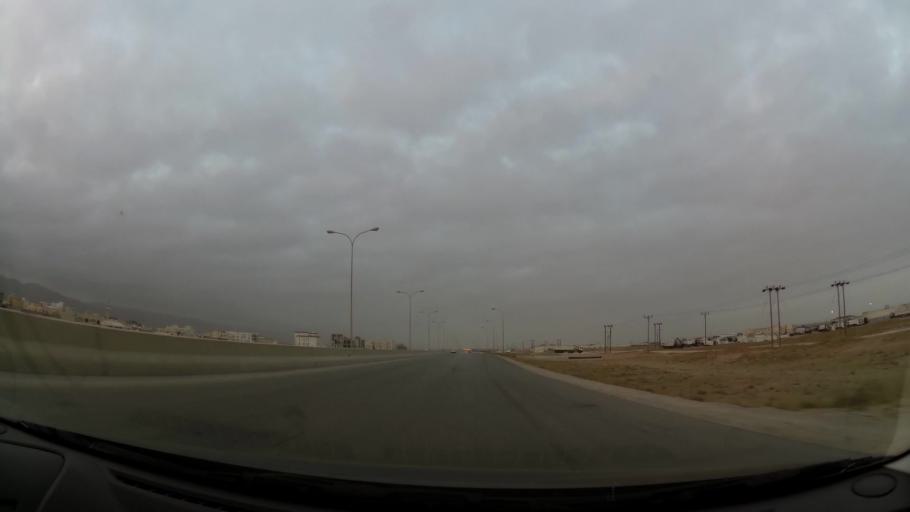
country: OM
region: Zufar
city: Salalah
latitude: 17.0367
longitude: 54.0401
